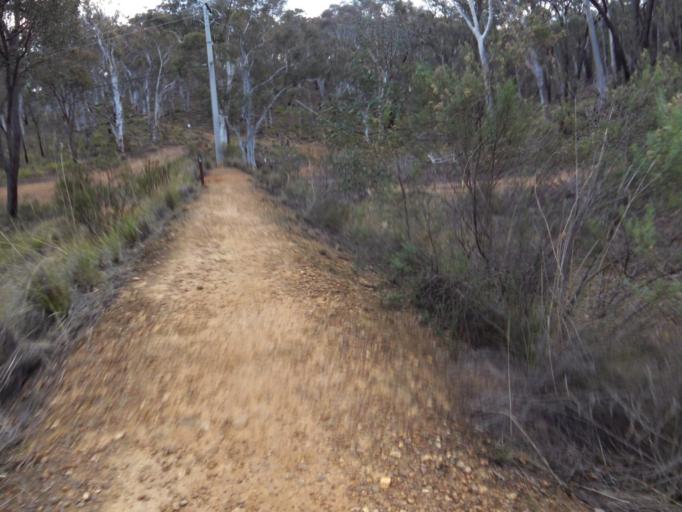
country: AU
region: Australian Capital Territory
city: Acton
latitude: -35.2685
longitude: 149.1087
